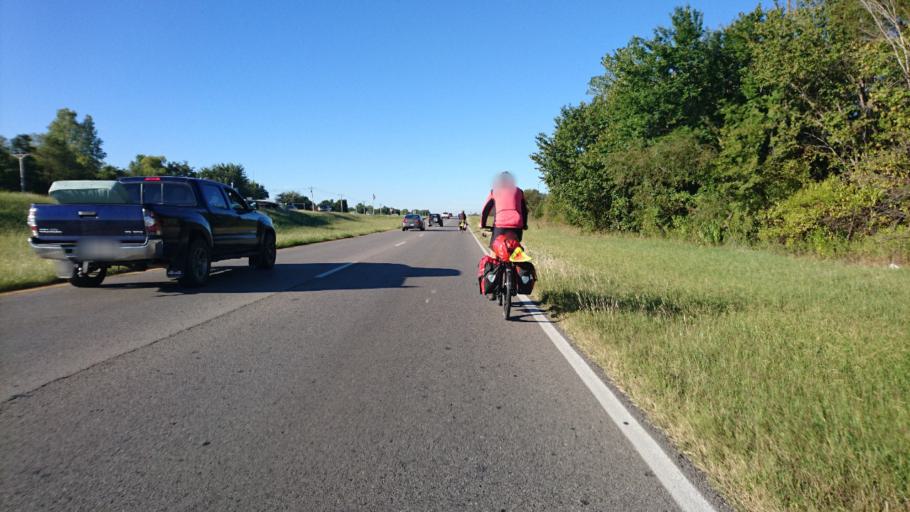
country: US
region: Oklahoma
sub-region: Rogers County
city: Claremore
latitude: 36.2706
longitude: -95.6461
